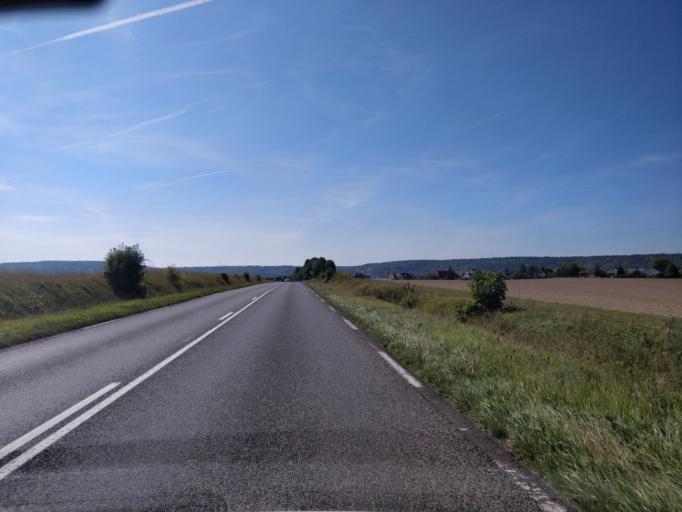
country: FR
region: Champagne-Ardenne
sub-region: Departement de l'Aube
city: Bouilly
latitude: 48.2054
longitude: 4.0049
